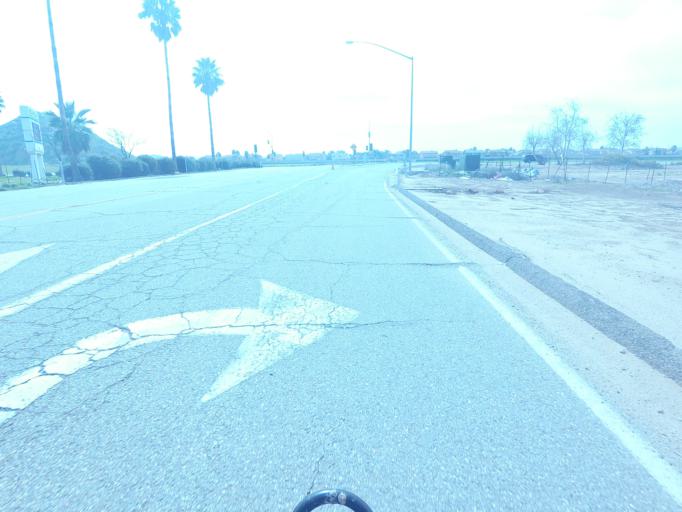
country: US
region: California
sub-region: Riverside County
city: Perris
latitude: 33.8456
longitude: -117.2043
